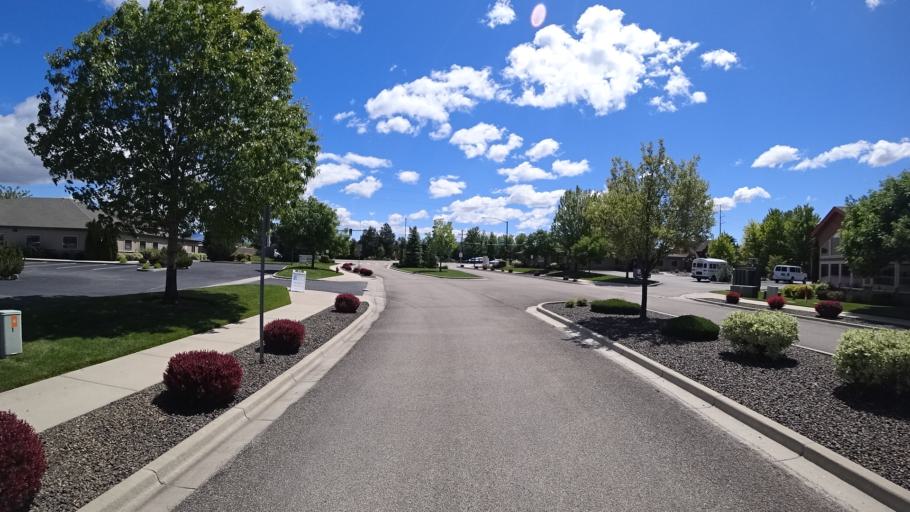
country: US
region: Idaho
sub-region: Ada County
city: Meridian
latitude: 43.6417
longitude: -116.3554
